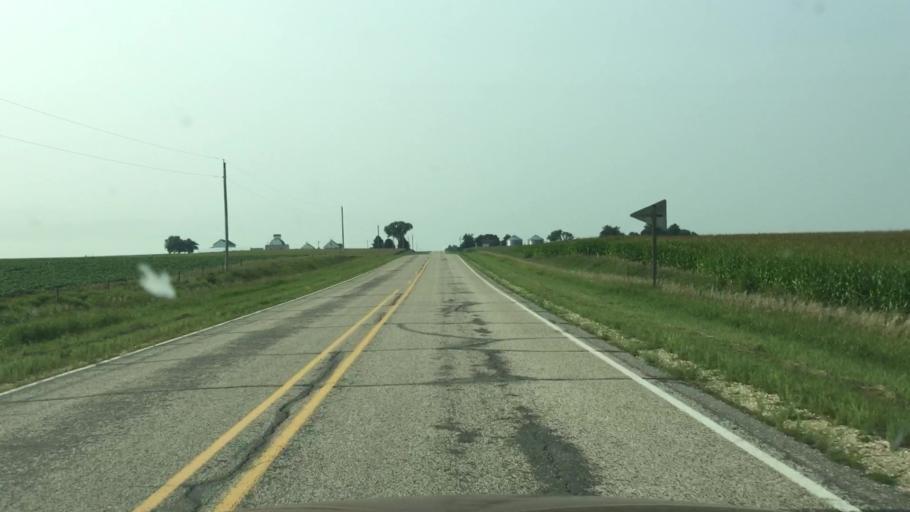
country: US
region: Iowa
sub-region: O'Brien County
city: Sheldon
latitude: 43.2747
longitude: -95.7829
